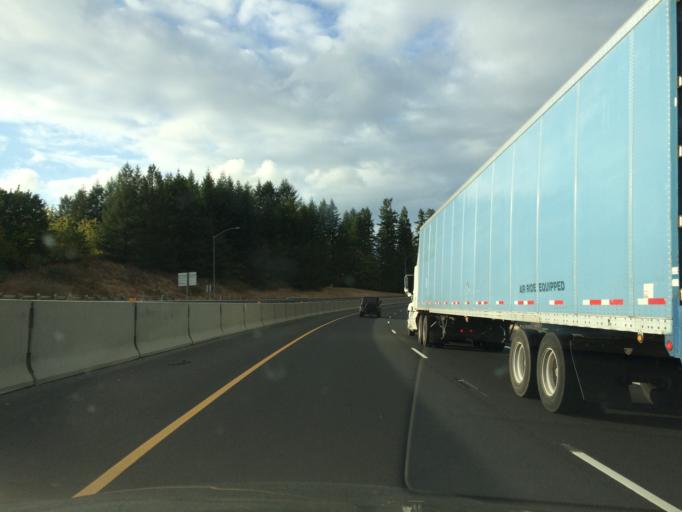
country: US
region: Oregon
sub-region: Douglas County
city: Drain
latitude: 43.7093
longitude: -123.2180
